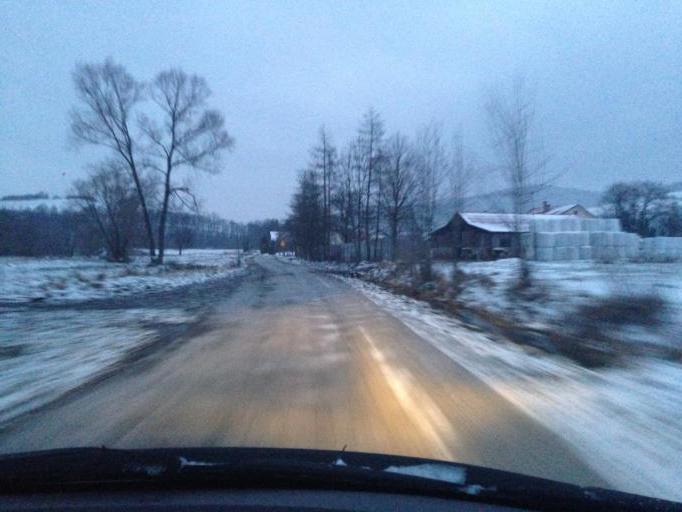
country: PL
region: Subcarpathian Voivodeship
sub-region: Powiat jasielski
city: Krempna
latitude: 49.5341
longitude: 21.5509
